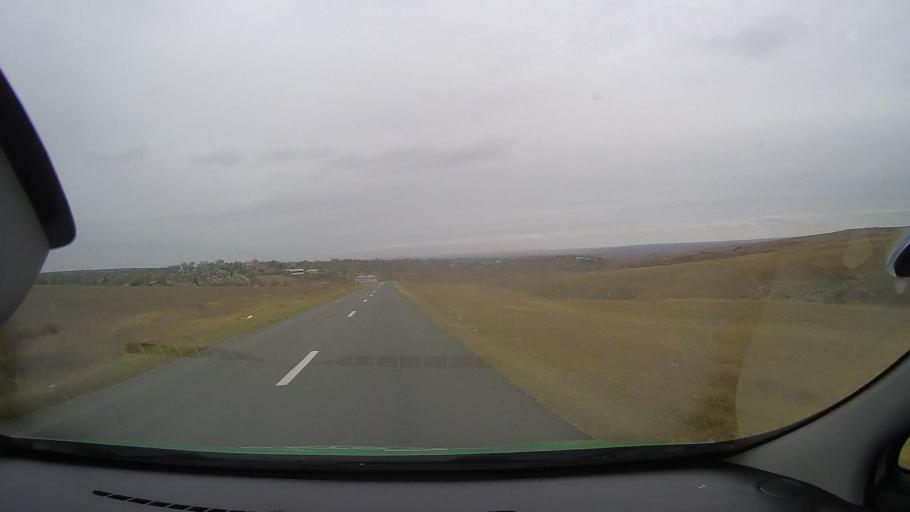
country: RO
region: Constanta
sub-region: Comuna Pantelimon
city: Pantelimon
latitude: 44.5377
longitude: 28.3280
